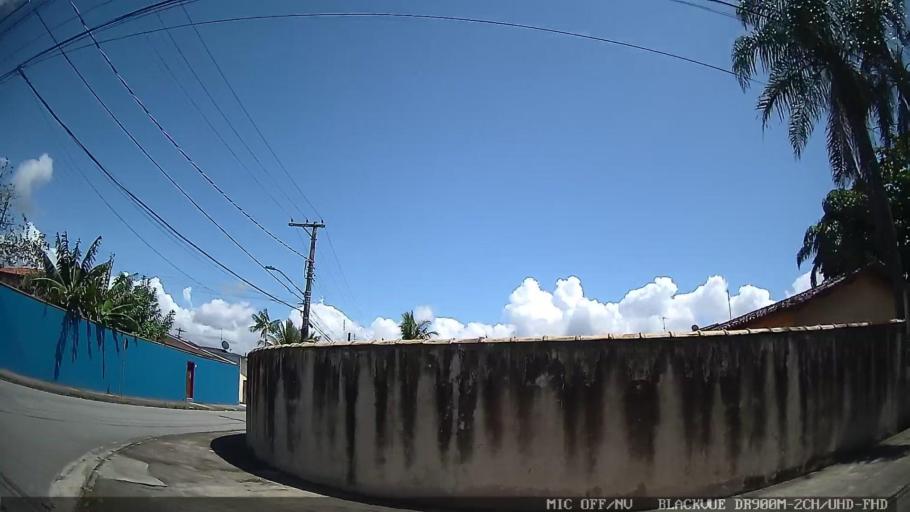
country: BR
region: Sao Paulo
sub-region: Caraguatatuba
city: Caraguatatuba
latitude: -23.6749
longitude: -45.4364
